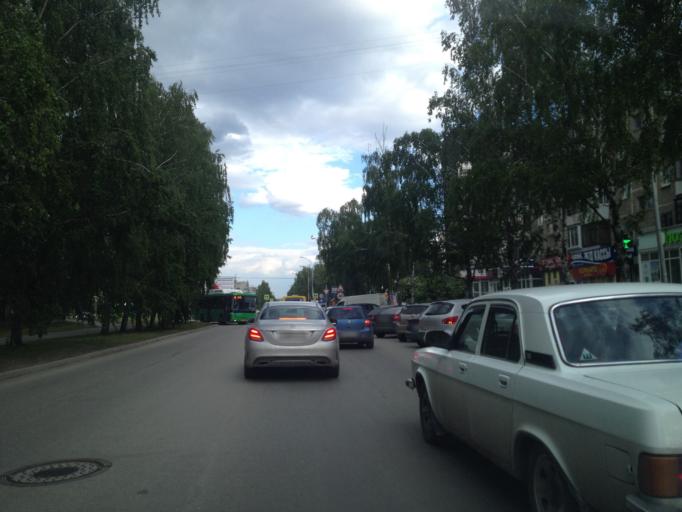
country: RU
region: Sverdlovsk
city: Sovkhoznyy
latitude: 56.8061
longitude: 60.5571
